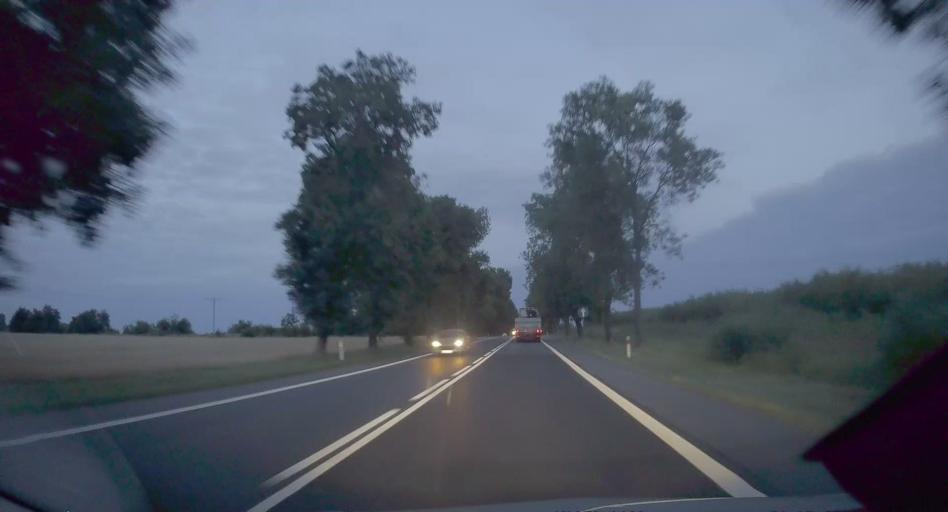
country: PL
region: Silesian Voivodeship
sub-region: Powiat klobucki
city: Klobuck
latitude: 50.9175
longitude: 18.8879
